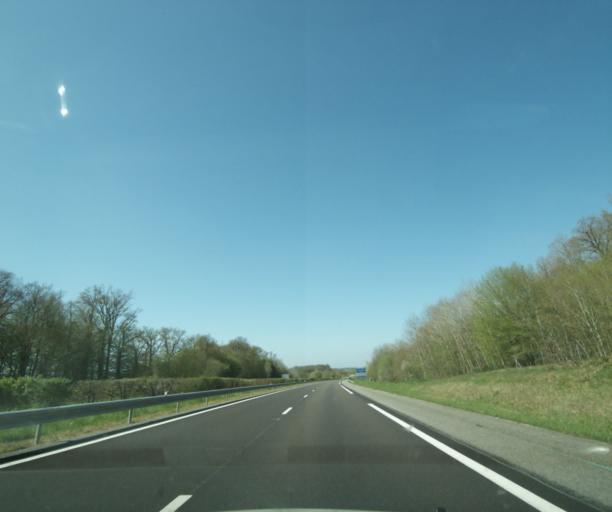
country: FR
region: Bourgogne
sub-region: Departement de la Nievre
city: Neuvy-sur-Loire
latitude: 47.5034
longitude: 2.9235
